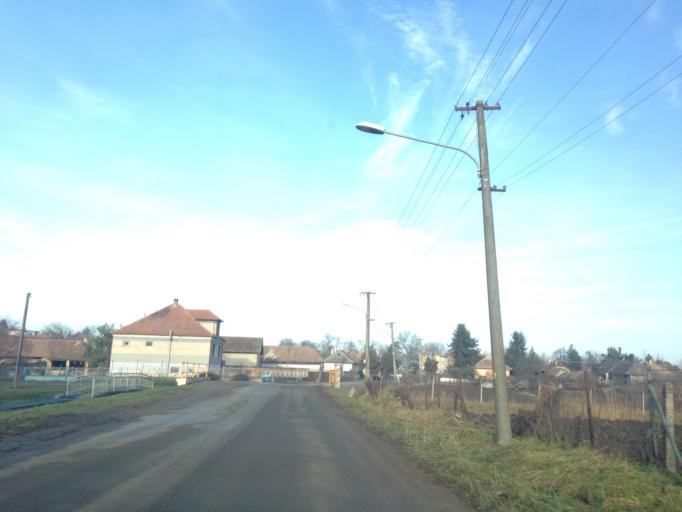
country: SK
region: Nitriansky
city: Svodin
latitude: 47.9536
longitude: 18.4128
